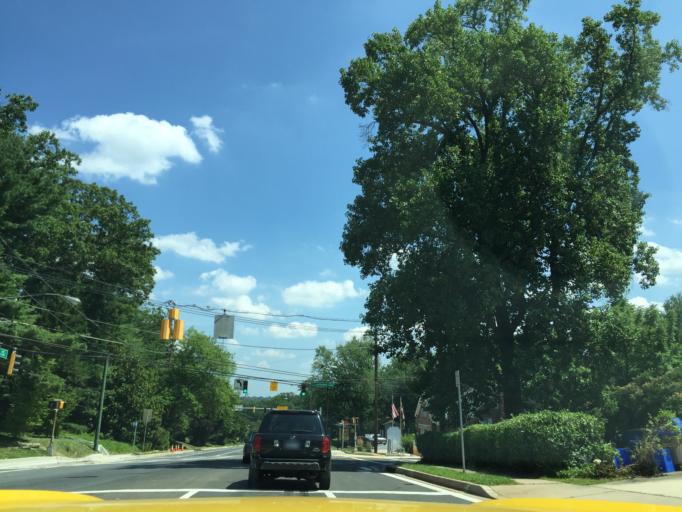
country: US
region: Maryland
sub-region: Montgomery County
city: Brookmont
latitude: 38.9638
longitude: -77.1216
